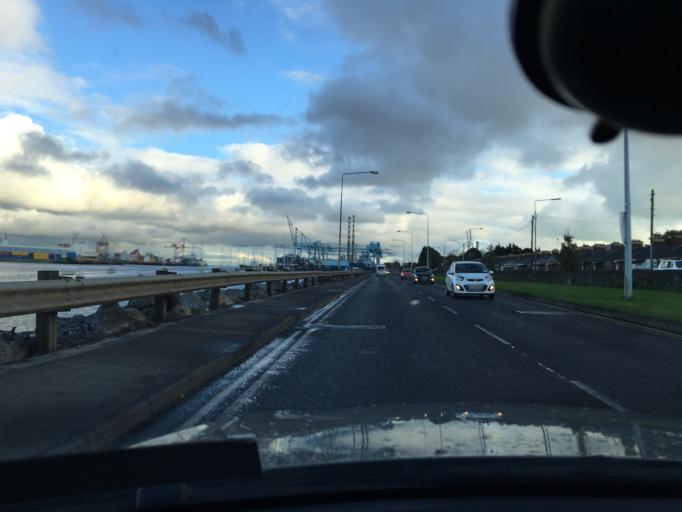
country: IE
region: Leinster
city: Ringsend
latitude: 53.3440
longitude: -6.2225
